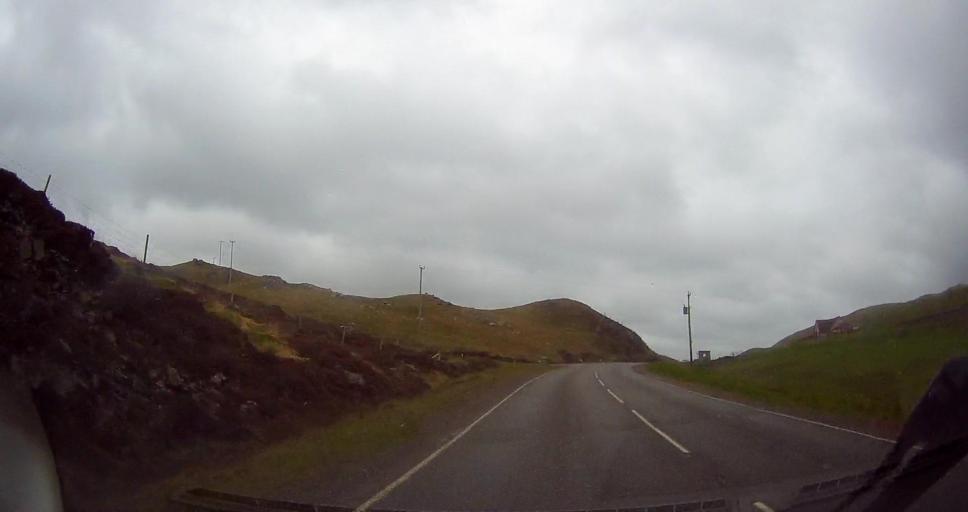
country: GB
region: Scotland
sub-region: Shetland Islands
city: Lerwick
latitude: 60.4067
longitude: -1.3879
